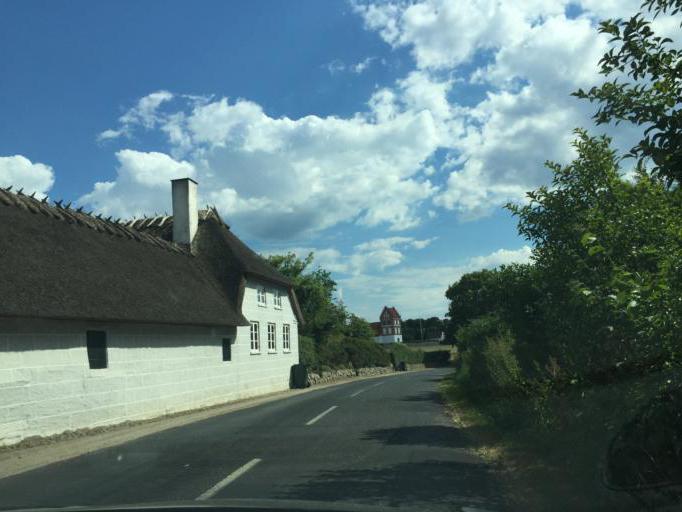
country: DK
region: South Denmark
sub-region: Assens Kommune
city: Harby
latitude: 55.1437
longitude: 10.0204
